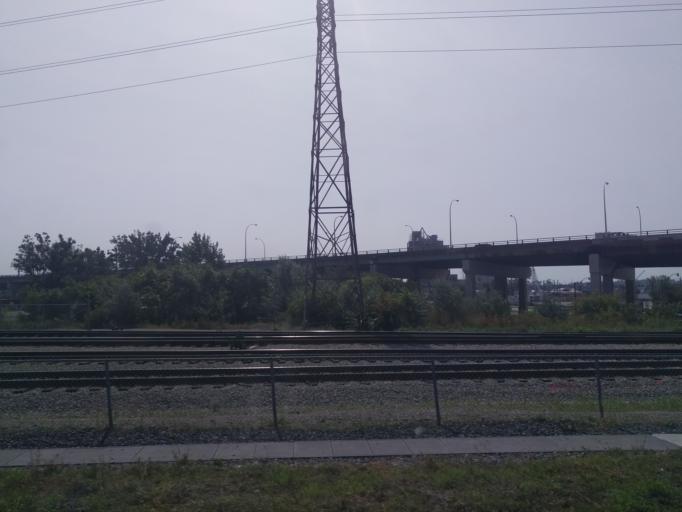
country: CA
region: Ontario
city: Toronto
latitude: 43.6501
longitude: -79.3561
